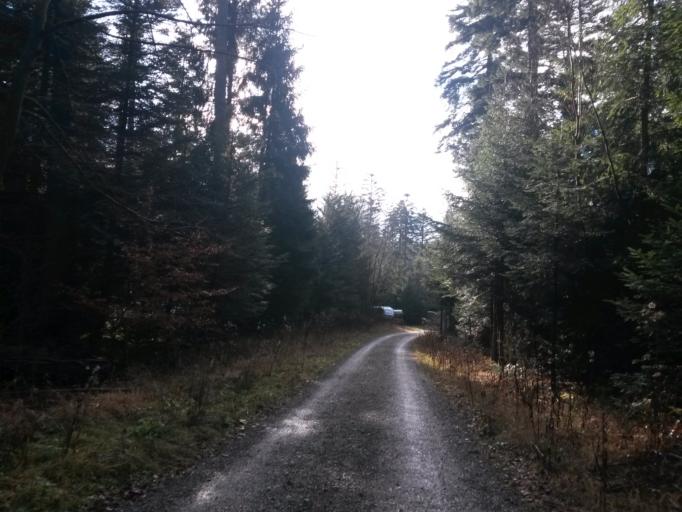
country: DE
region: Baden-Wuerttemberg
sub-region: Karlsruhe Region
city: Pfalzgrafenweiler
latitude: 48.5108
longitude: 8.5239
